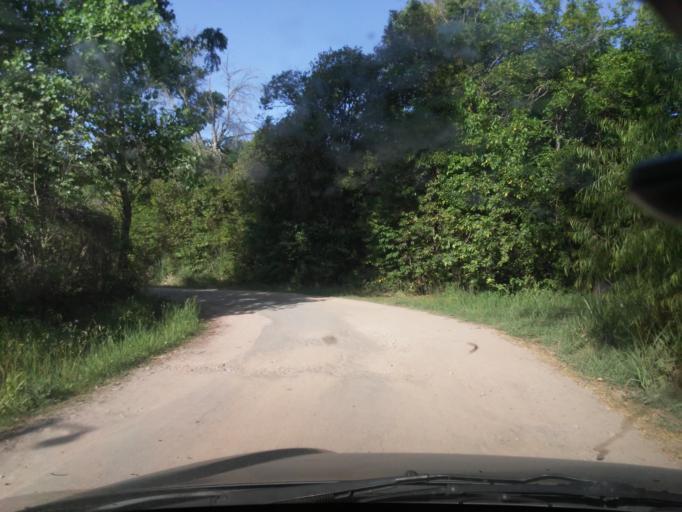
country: AR
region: Buenos Aires
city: Belen de Escobar
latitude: -34.2498
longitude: -58.7252
